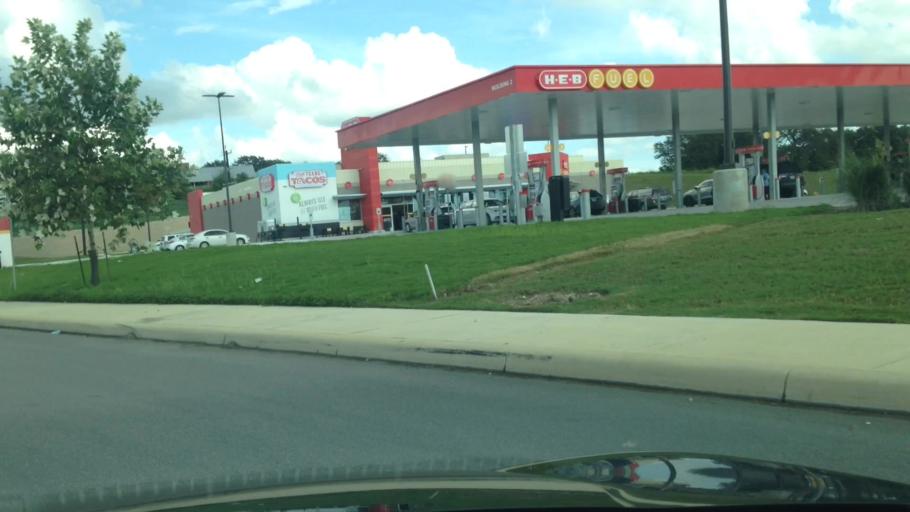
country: US
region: Texas
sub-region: Bexar County
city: Hollywood Park
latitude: 29.5972
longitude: -98.4178
